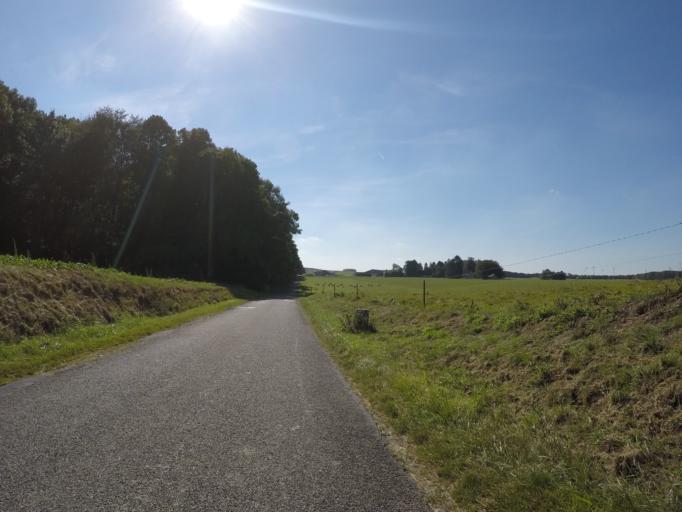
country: BE
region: Wallonia
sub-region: Province de Namur
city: Assesse
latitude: 50.3054
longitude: 5.0311
